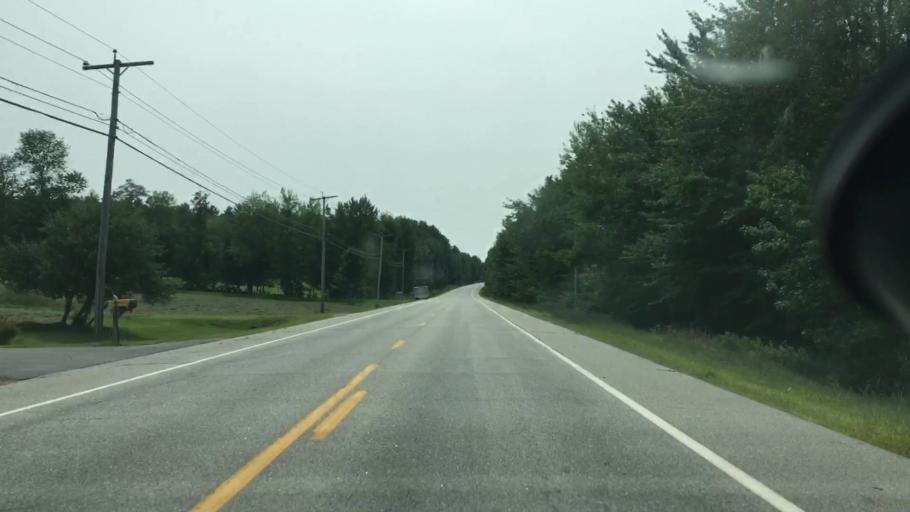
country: US
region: Maine
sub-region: Androscoggin County
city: Livermore Falls
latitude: 44.4363
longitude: -70.1475
